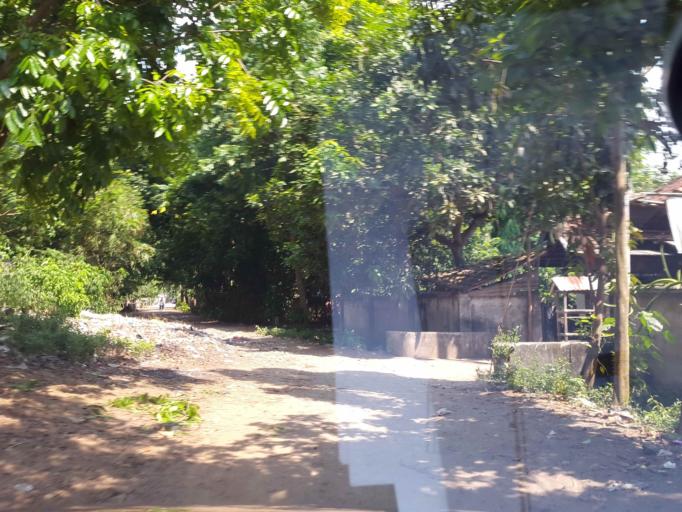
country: ID
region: West Nusa Tenggara
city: Jelateng Timur
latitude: -8.6830
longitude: 116.0912
